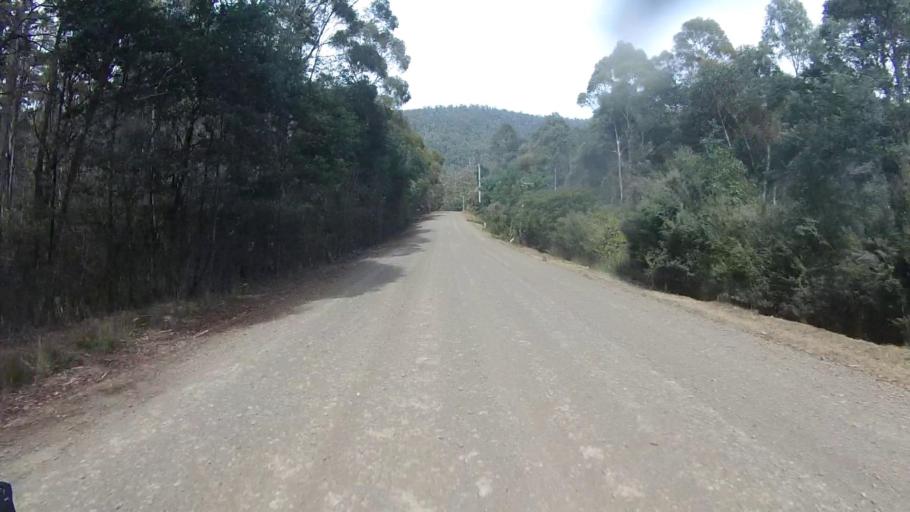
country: AU
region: Tasmania
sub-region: Sorell
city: Sorell
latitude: -42.6889
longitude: 147.8692
